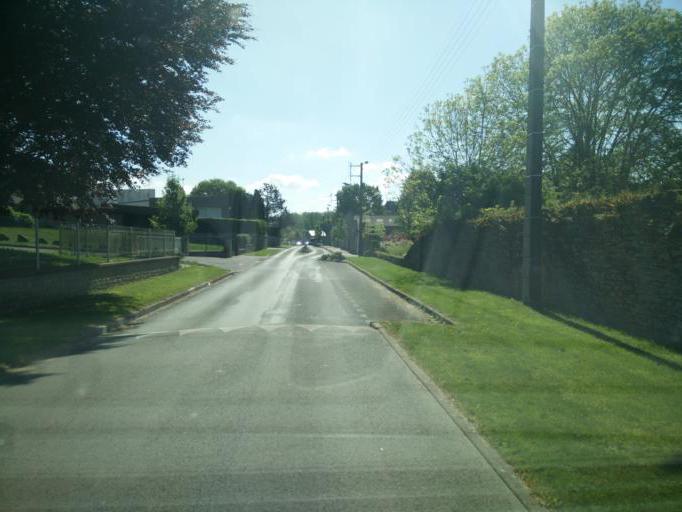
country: FR
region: Brittany
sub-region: Departement du Morbihan
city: Josselin
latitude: 47.9536
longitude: -2.5618
